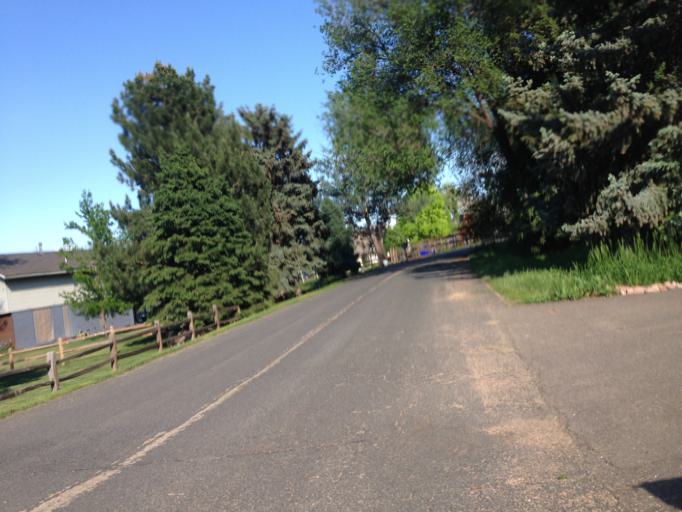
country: US
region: Colorado
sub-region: Boulder County
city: Lafayette
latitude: 40.0166
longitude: -105.1052
